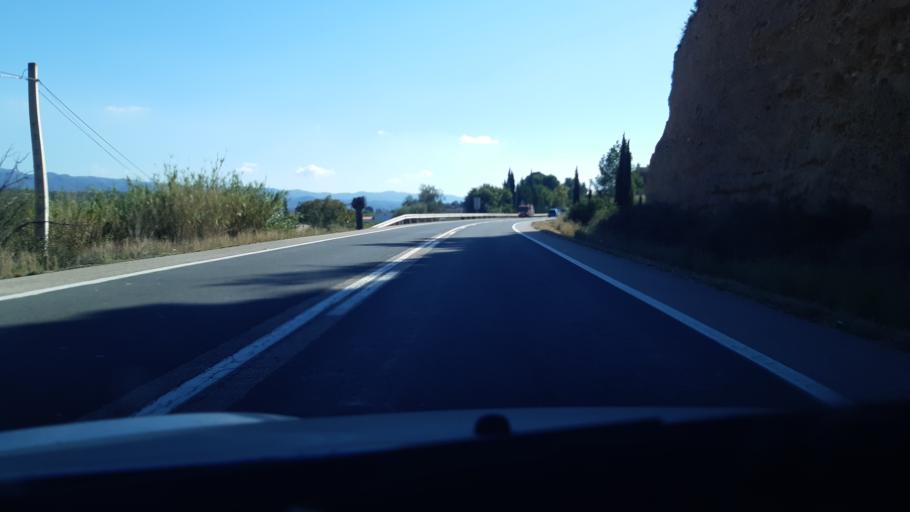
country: ES
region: Catalonia
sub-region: Provincia de Tarragona
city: Tivenys
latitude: 40.8962
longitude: 0.4881
